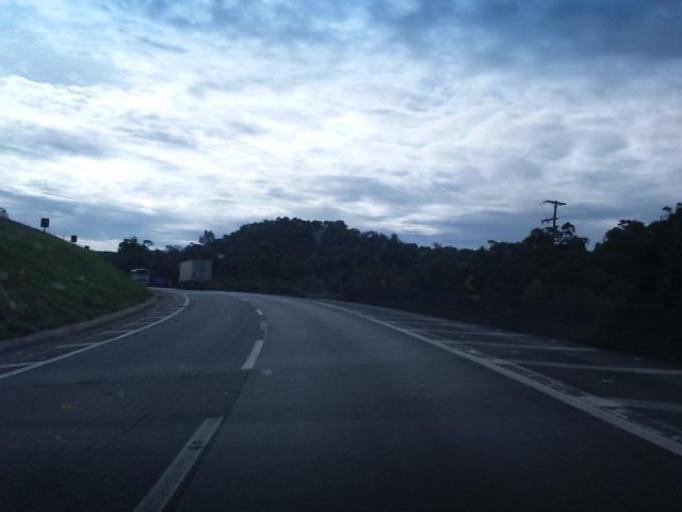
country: BR
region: Parana
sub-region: Antonina
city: Antonina
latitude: -25.0982
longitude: -48.6802
